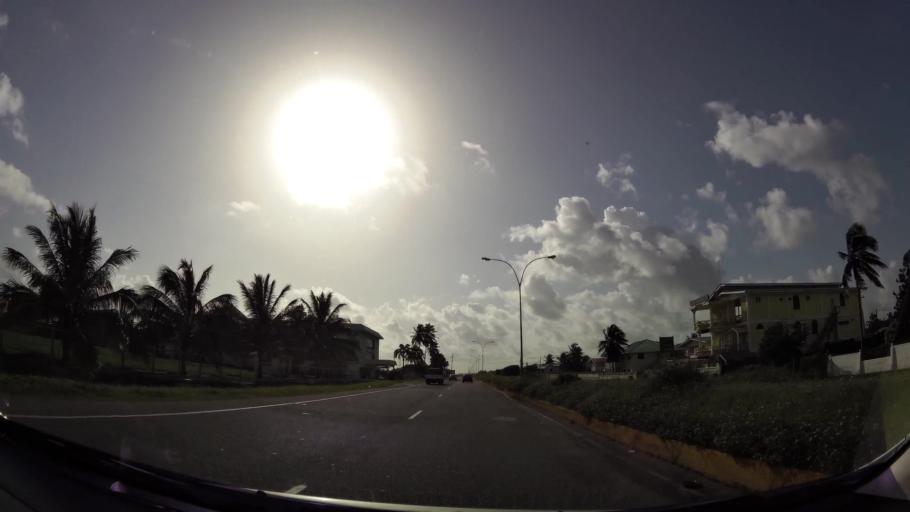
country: GY
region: Demerara-Mahaica
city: Georgetown
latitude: 6.8262
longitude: -58.1216
